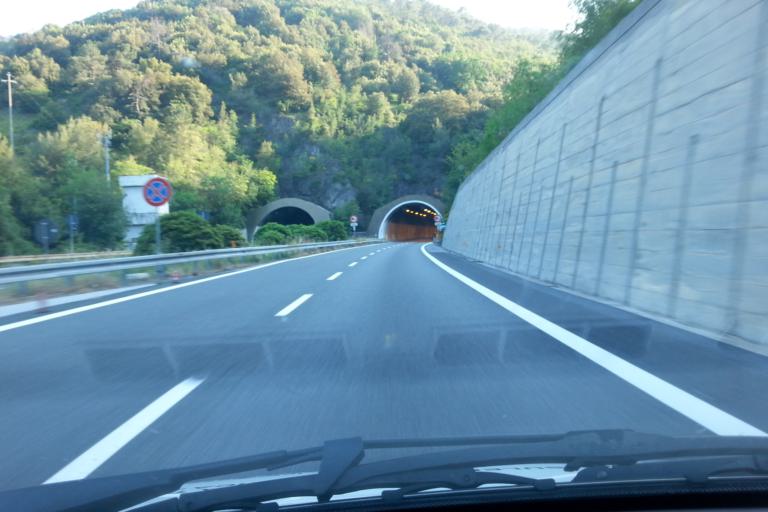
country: IT
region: Liguria
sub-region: Provincia di Savona
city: Borgio
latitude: 44.1741
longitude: 8.2933
